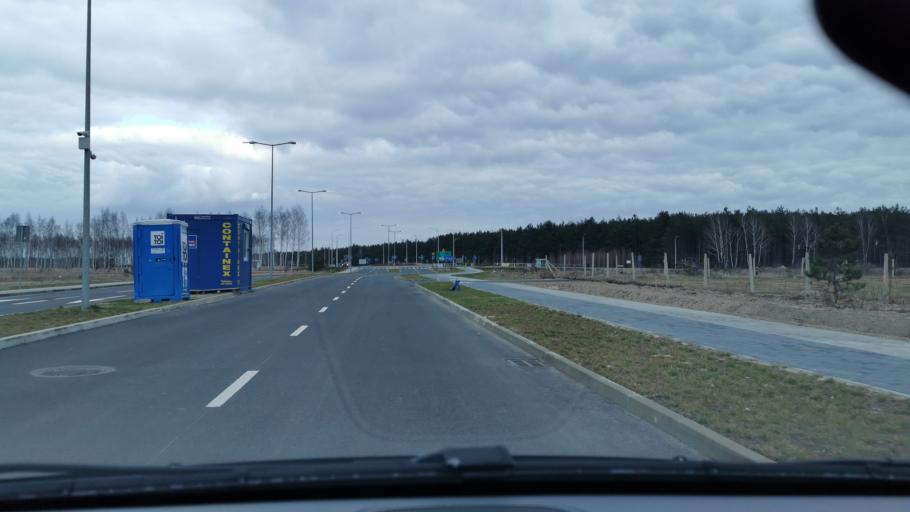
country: PL
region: Masovian Voivodeship
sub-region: Powiat zyrardowski
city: Mszczonow
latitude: 51.9893
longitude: 20.4622
